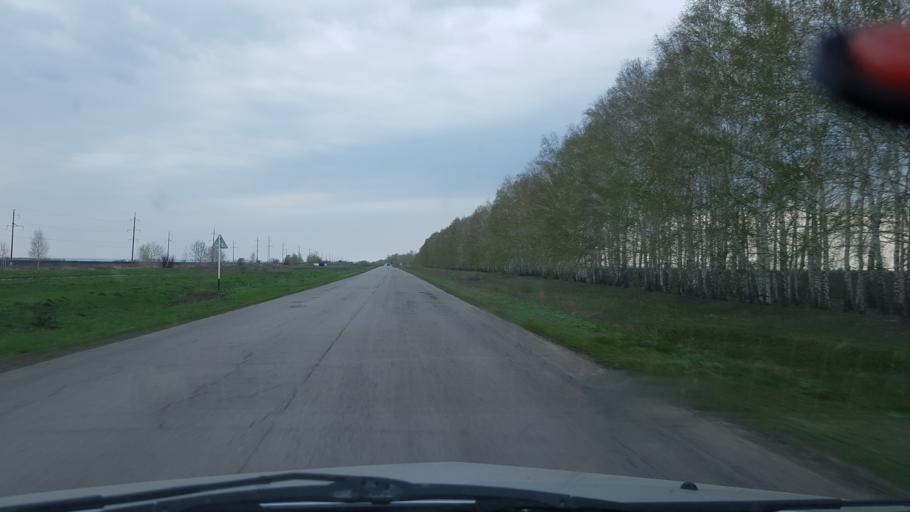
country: RU
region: Samara
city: Podstepki
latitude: 53.6664
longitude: 49.1602
